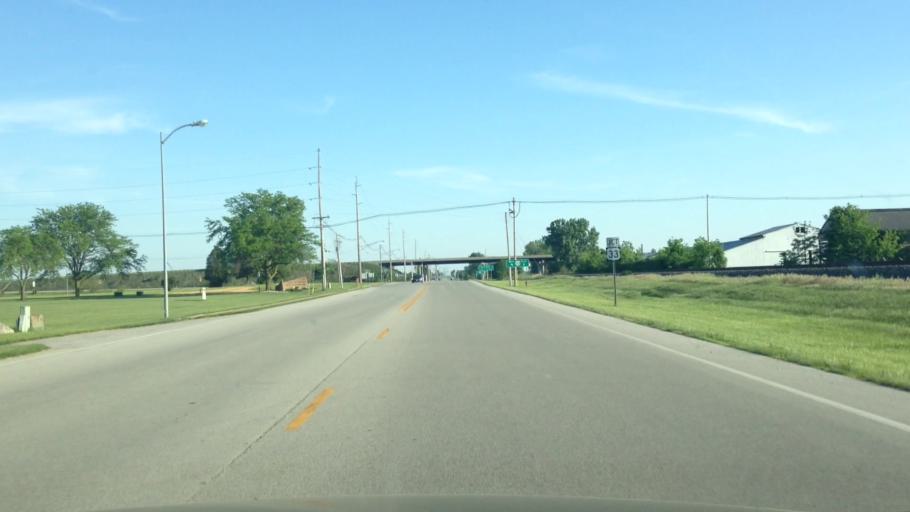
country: US
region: Ohio
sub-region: Auglaize County
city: Wapakoneta
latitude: 40.5596
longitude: -84.1941
